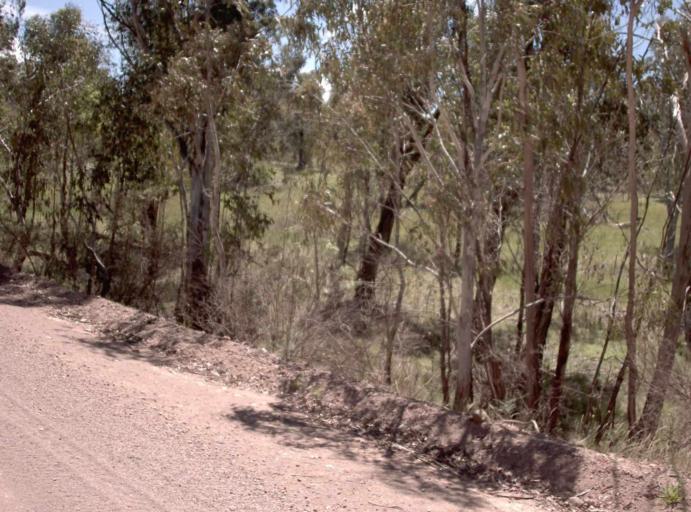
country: AU
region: New South Wales
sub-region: Snowy River
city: Jindabyne
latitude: -37.0330
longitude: 148.2737
